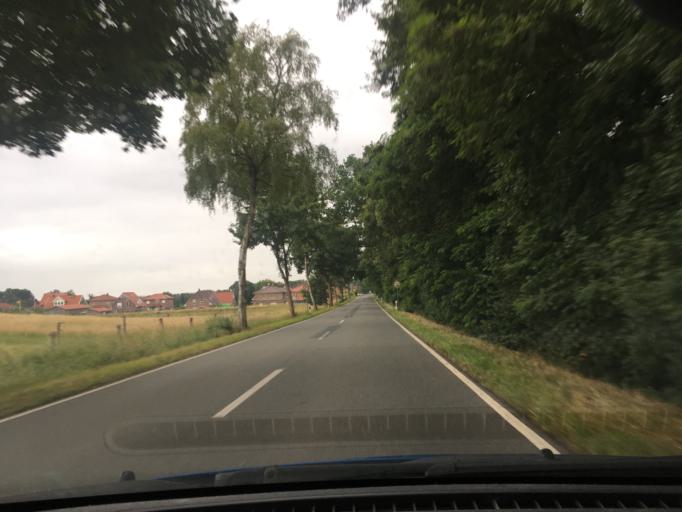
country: DE
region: Lower Saxony
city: Egestorf
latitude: 53.2005
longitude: 10.0666
